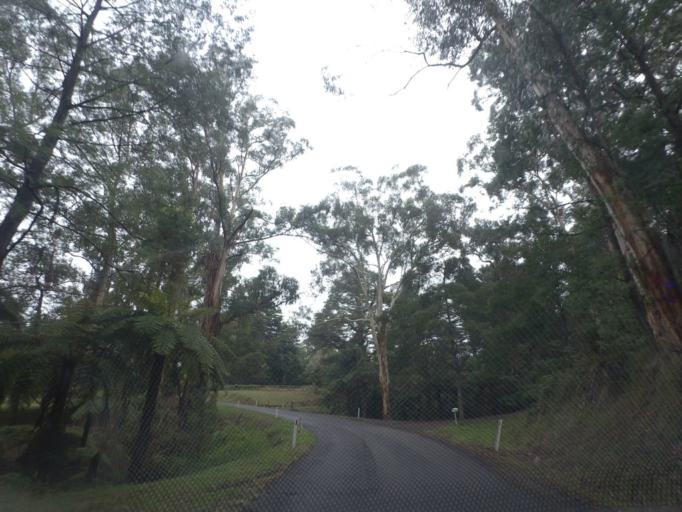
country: AU
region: Victoria
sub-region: Yarra Ranges
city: Yarra Junction
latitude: -37.7343
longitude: 145.5946
